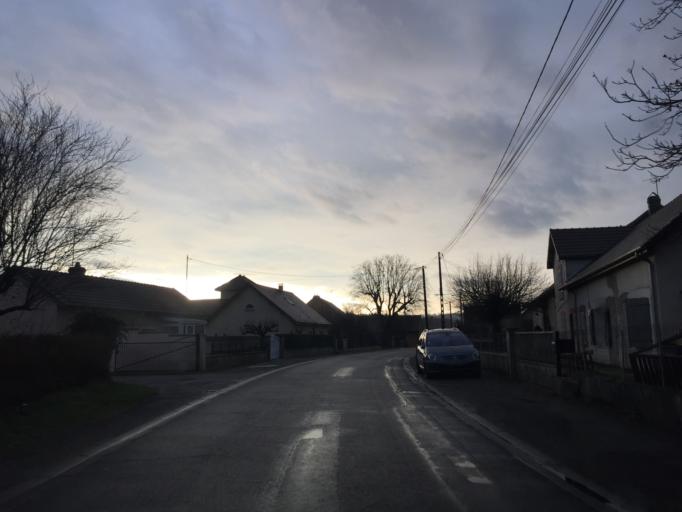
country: FR
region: Franche-Comte
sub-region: Departement du Jura
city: Choisey
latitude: 47.0207
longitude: 5.4871
